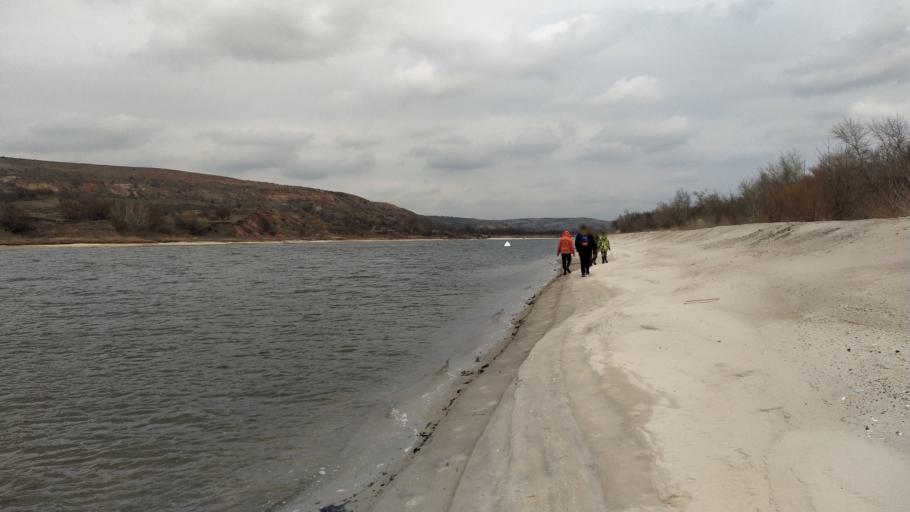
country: RU
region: Rostov
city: Semikarakorsk
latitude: 47.5550
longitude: 40.6724
